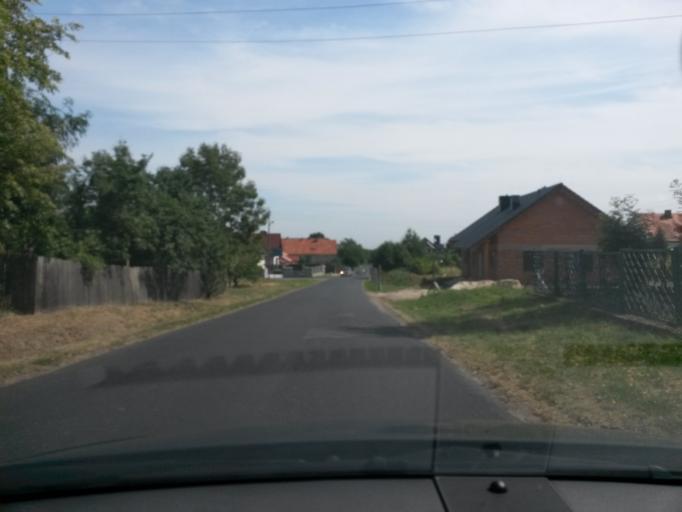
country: PL
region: Lower Silesian Voivodeship
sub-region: Powiat jaworski
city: Paszowice
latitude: 51.0081
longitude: 16.1460
